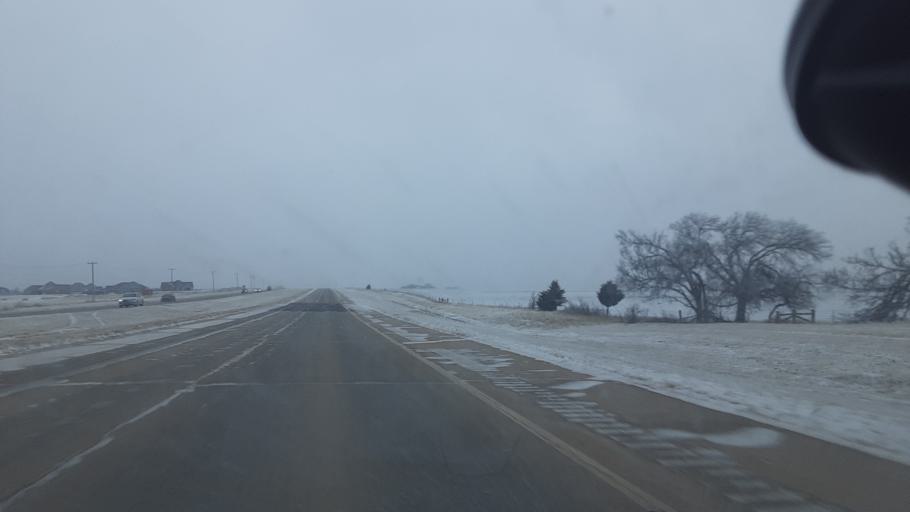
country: US
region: Oklahoma
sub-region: Logan County
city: Langston
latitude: 35.9271
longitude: -97.3198
